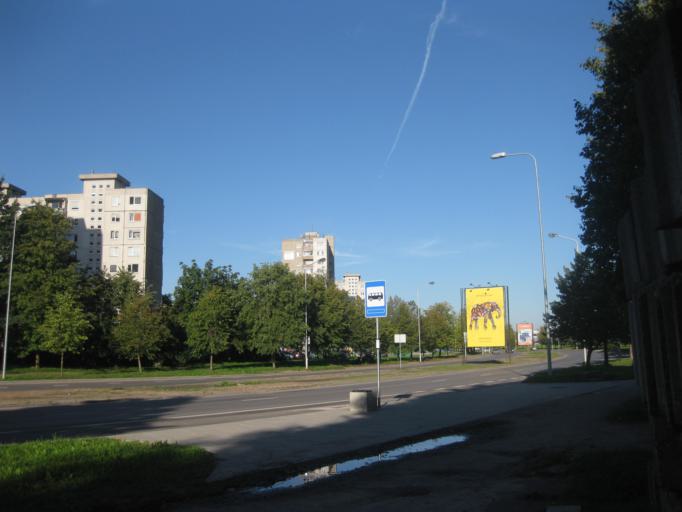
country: LT
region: Kauno apskritis
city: Dainava (Kaunas)
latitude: 54.9292
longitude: 23.9712
